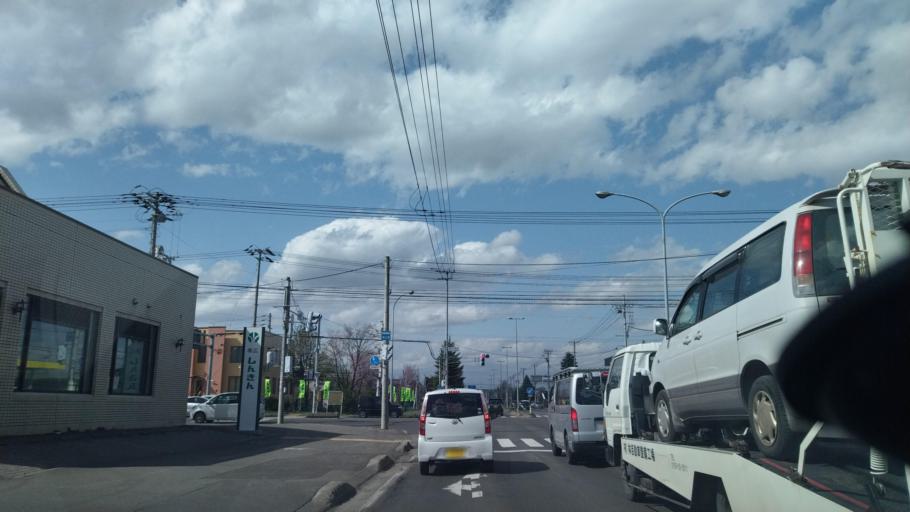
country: JP
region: Hokkaido
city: Obihiro
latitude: 42.9173
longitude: 143.1445
